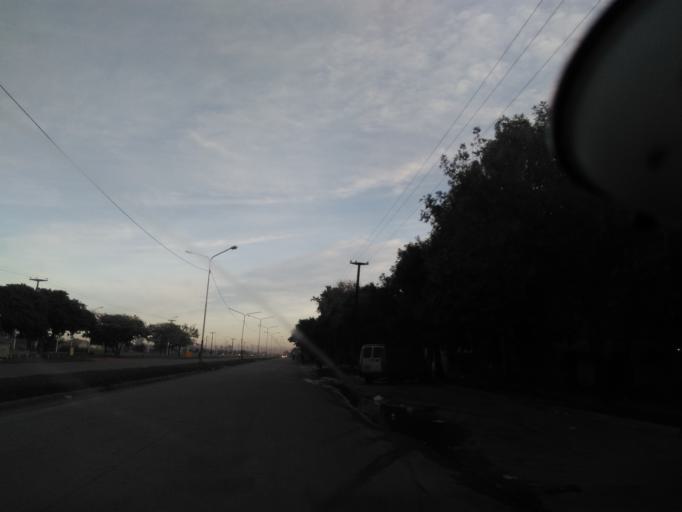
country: AR
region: Chaco
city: Resistencia
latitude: -27.4695
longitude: -59.0089
